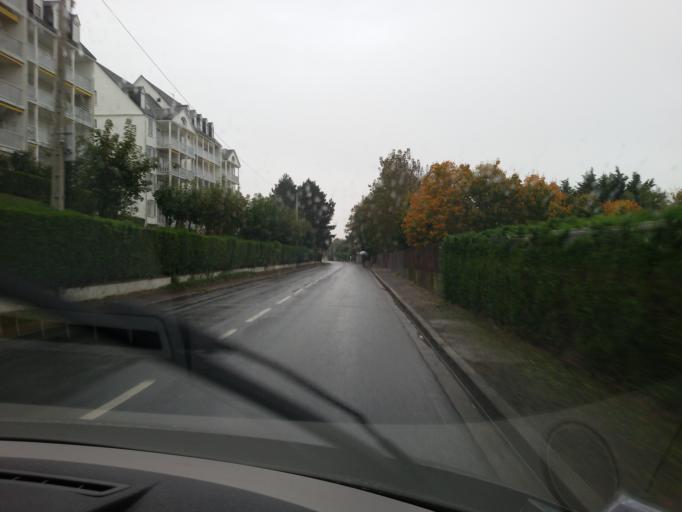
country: FR
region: Lower Normandy
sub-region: Departement du Calvados
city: Trouville-sur-Mer
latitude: 49.3718
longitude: 0.0860
